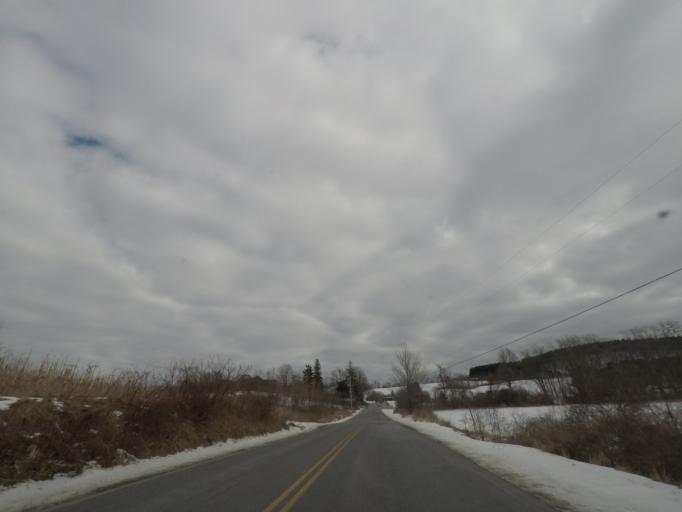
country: US
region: New York
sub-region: Rensselaer County
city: Hoosick Falls
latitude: 42.8743
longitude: -73.4049
